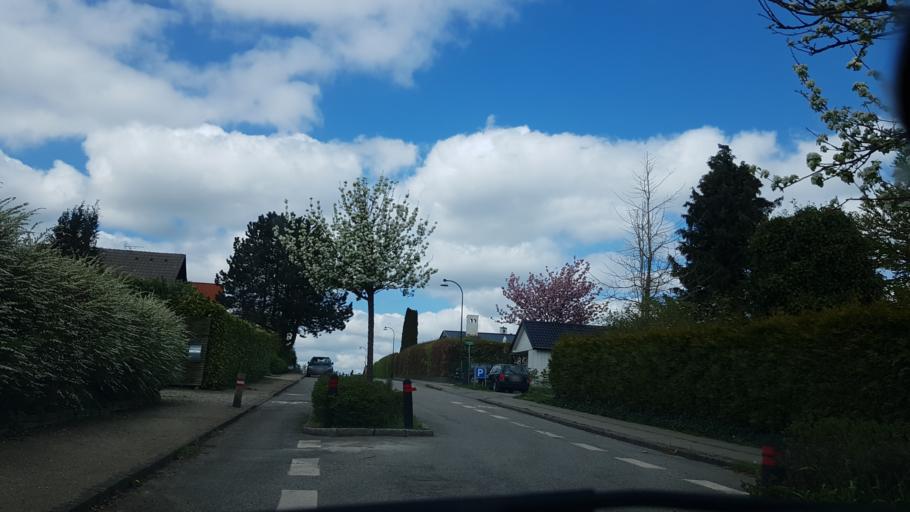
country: DK
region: Capital Region
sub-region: Rudersdal Kommune
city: Trorod
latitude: 55.8439
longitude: 12.5419
